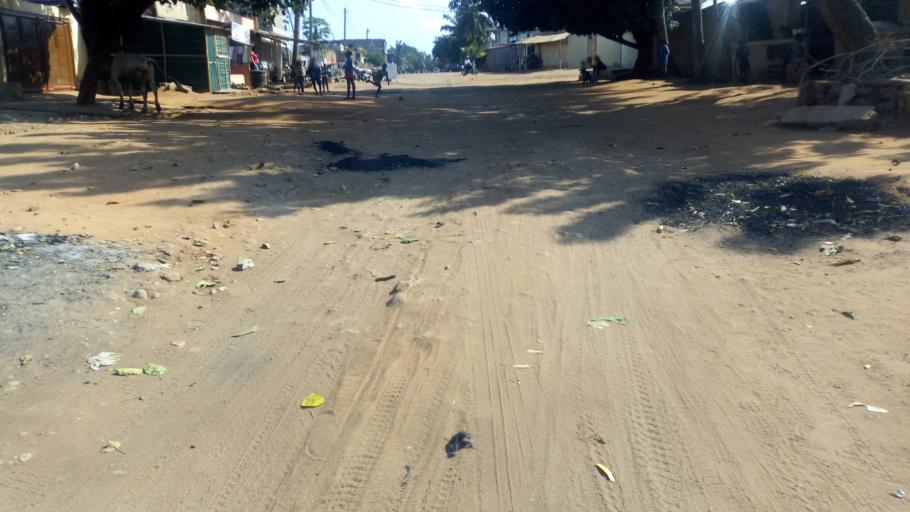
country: TG
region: Maritime
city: Lome
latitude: 6.2272
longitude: 1.1806
